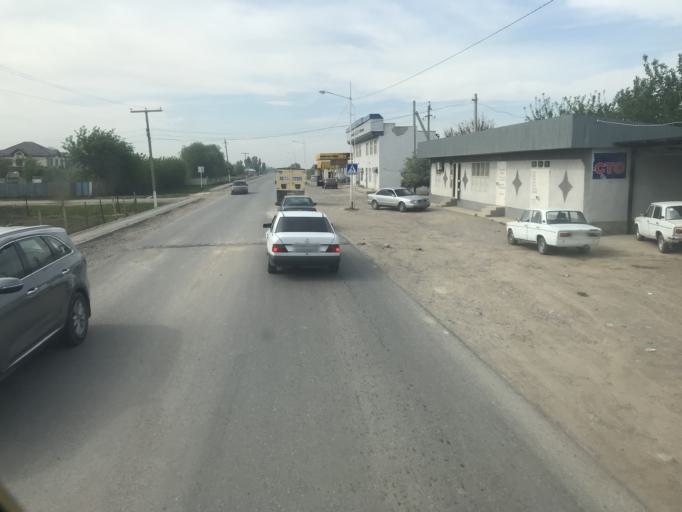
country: KZ
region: Ongtustik Qazaqstan
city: Asykata
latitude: 41.0033
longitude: 68.2141
